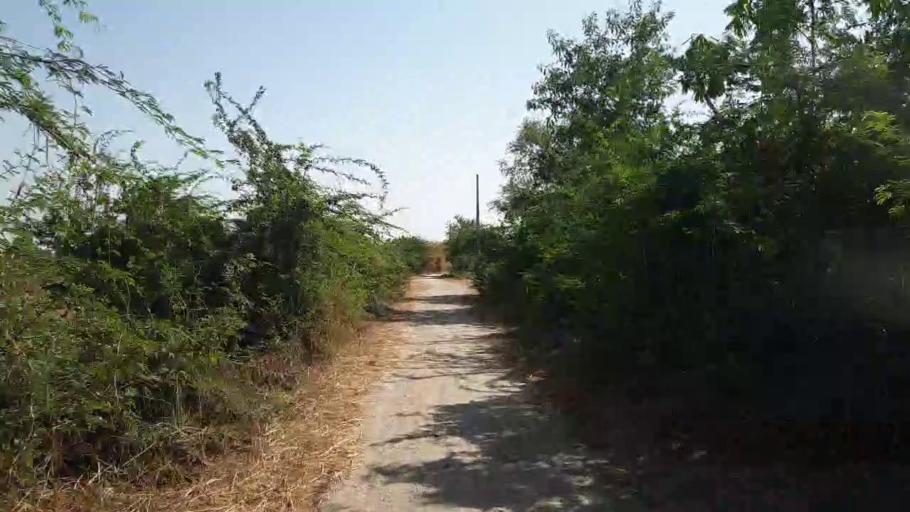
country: PK
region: Sindh
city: Tando Bago
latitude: 24.6373
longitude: 68.9914
